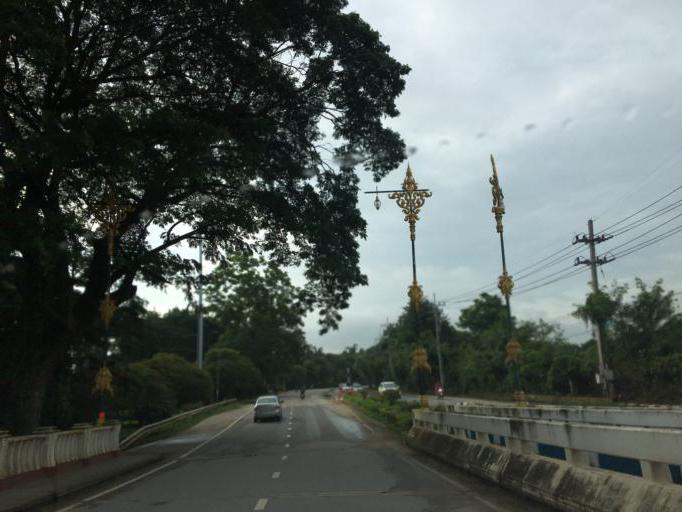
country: TH
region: Chiang Rai
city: Chiang Rai
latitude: 19.9216
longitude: 99.8192
